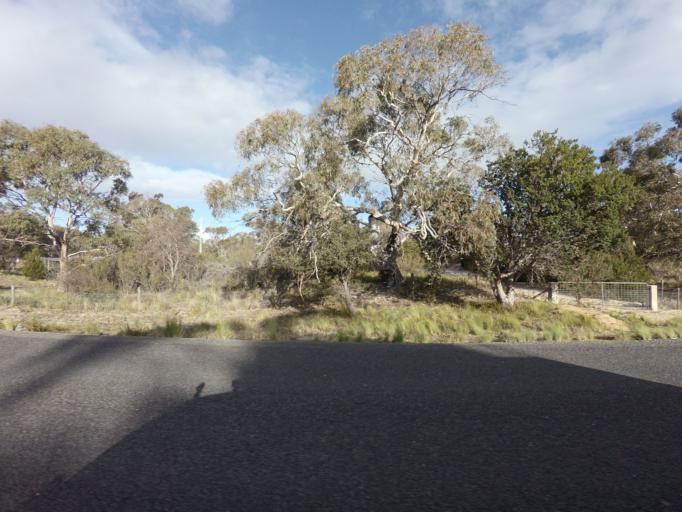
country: AU
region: Tasmania
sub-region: Break O'Day
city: St Helens
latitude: -42.0926
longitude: 148.2207
